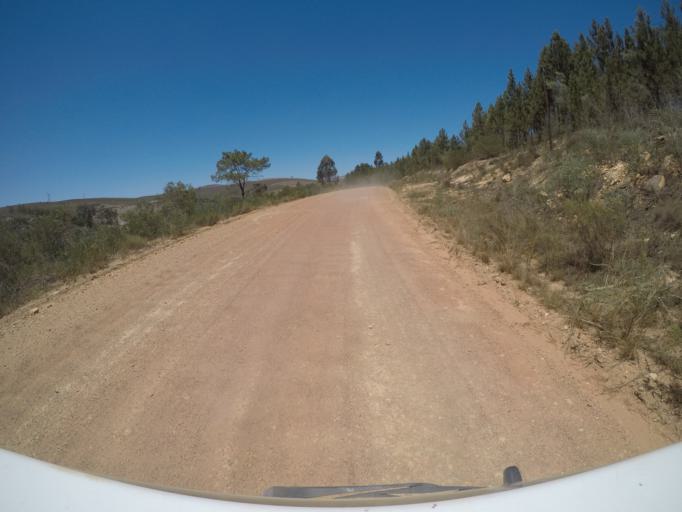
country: ZA
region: Western Cape
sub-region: Overberg District Municipality
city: Caledon
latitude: -34.1851
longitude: 19.2232
